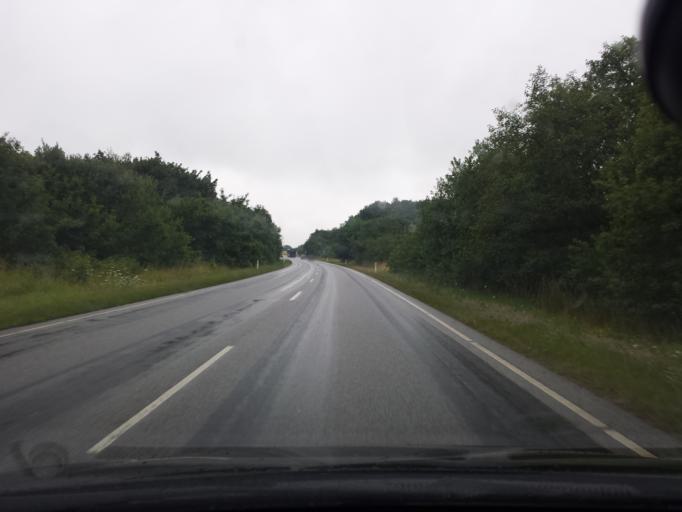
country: DK
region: South Denmark
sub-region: Sonderborg Kommune
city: Dybbol
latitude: 54.9162
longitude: 9.7105
